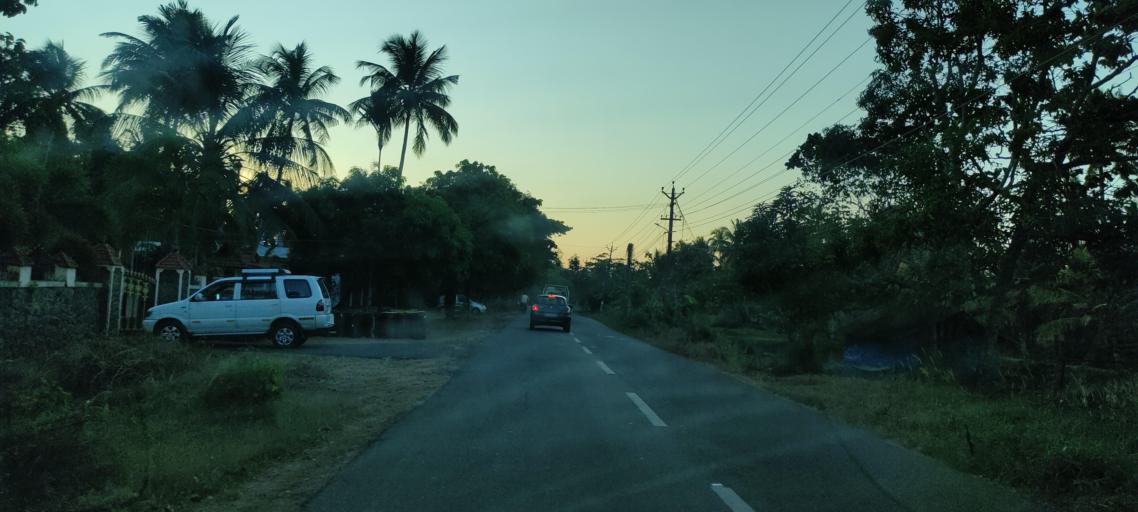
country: IN
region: Kerala
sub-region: Alappuzha
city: Kayankulam
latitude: 9.2576
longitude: 76.4203
